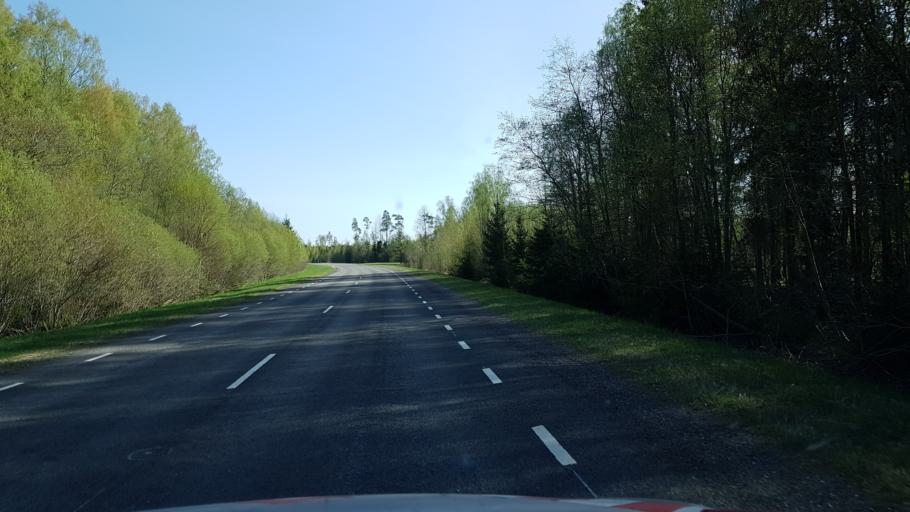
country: EE
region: Viljandimaa
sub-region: Karksi vald
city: Karksi-Nuia
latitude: 58.2184
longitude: 25.5639
